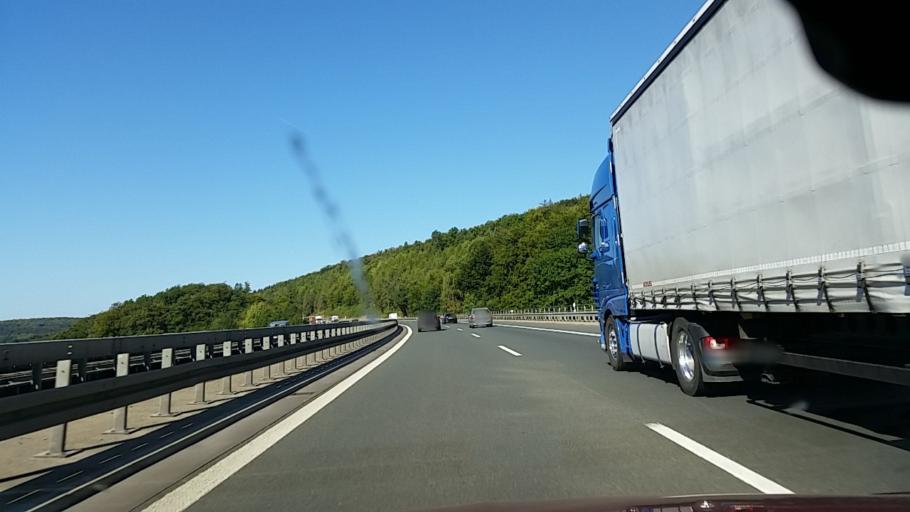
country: DE
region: Bavaria
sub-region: Regierungsbezirk Unterfranken
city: Bad Bruckenau
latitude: 50.3236
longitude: 9.8212
